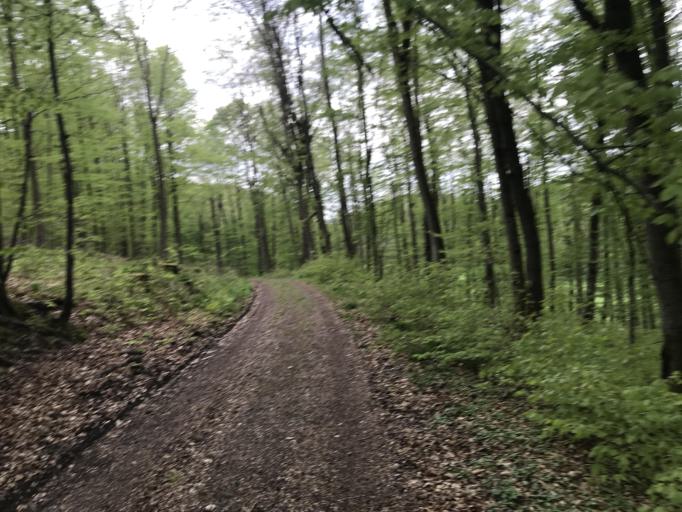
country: DE
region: Hesse
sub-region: Regierungsbezirk Giessen
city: Laubach
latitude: 50.5181
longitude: 8.9894
